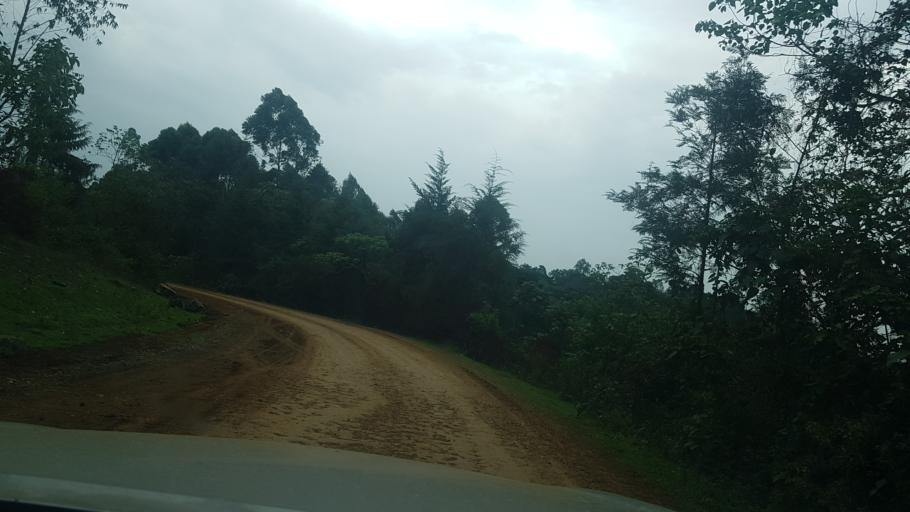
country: ET
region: Oromiya
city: Gore
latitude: 7.9099
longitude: 35.5117
